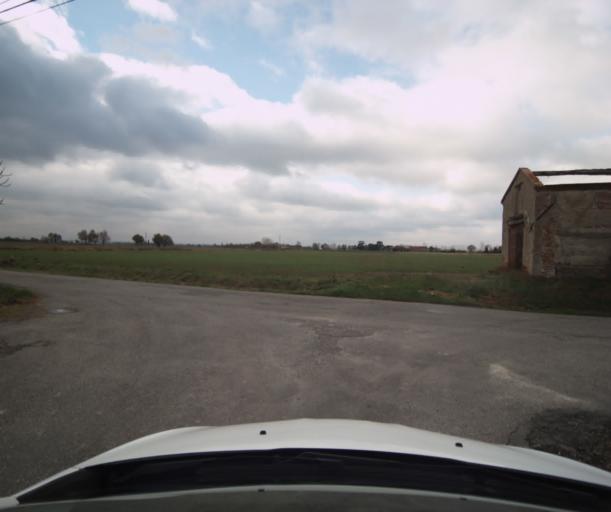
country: FR
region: Midi-Pyrenees
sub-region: Departement du Tarn-et-Garonne
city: Castelsarrasin
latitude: 44.0546
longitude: 1.1486
